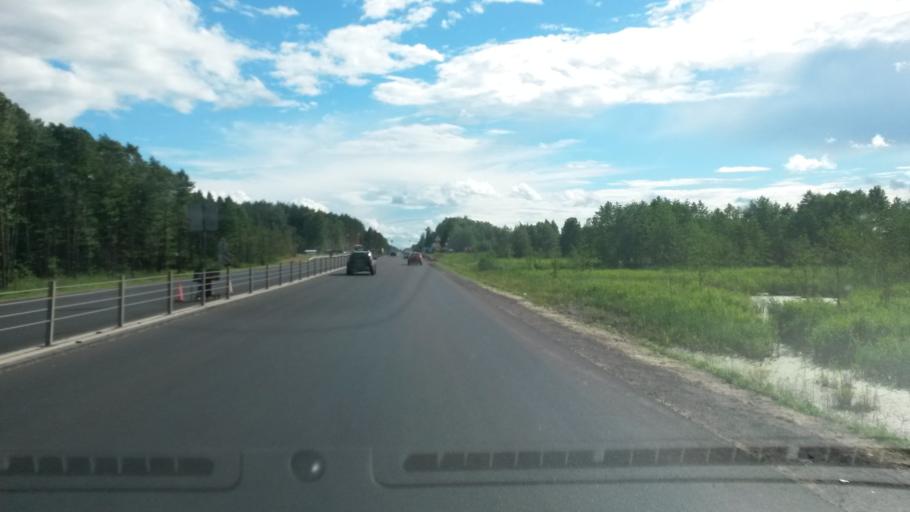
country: RU
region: Jaroslavl
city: Semibratovo
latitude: 57.2507
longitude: 39.4821
